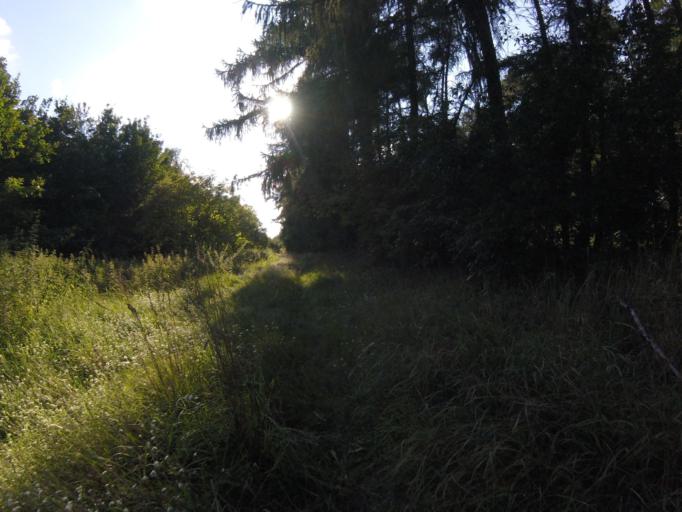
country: DE
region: Brandenburg
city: Schulzendorf
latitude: 52.3180
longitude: 13.5652
